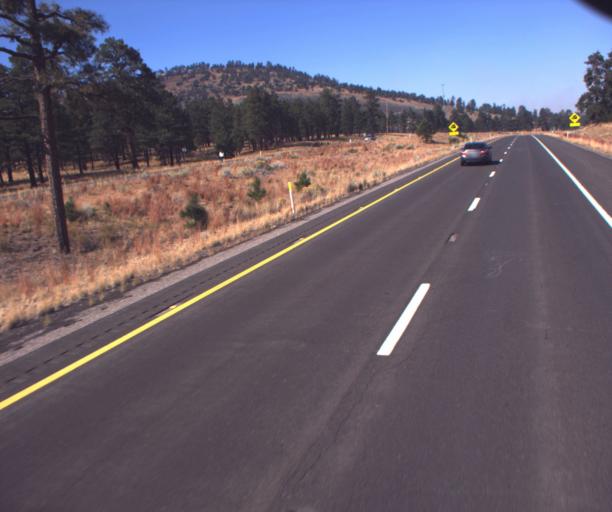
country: US
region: Arizona
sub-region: Coconino County
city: Flagstaff
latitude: 35.3782
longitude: -111.5790
